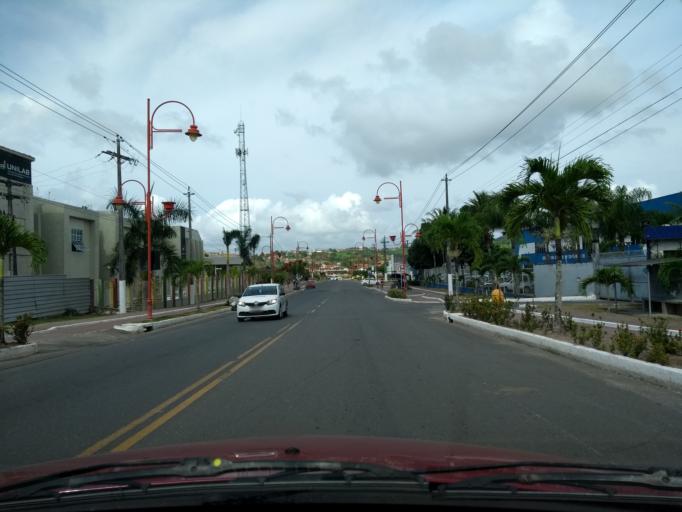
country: BR
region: Bahia
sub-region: Sao Francisco Do Conde
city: Sao Francisco do Conde
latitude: -12.6159
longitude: -38.6623
